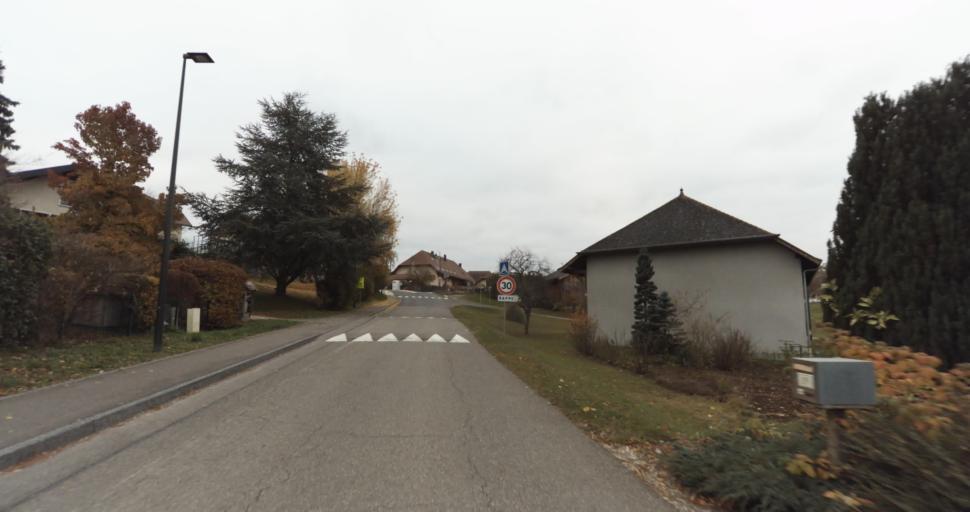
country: FR
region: Rhone-Alpes
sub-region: Departement de la Haute-Savoie
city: Chavanod
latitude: 45.8624
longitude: 6.0448
